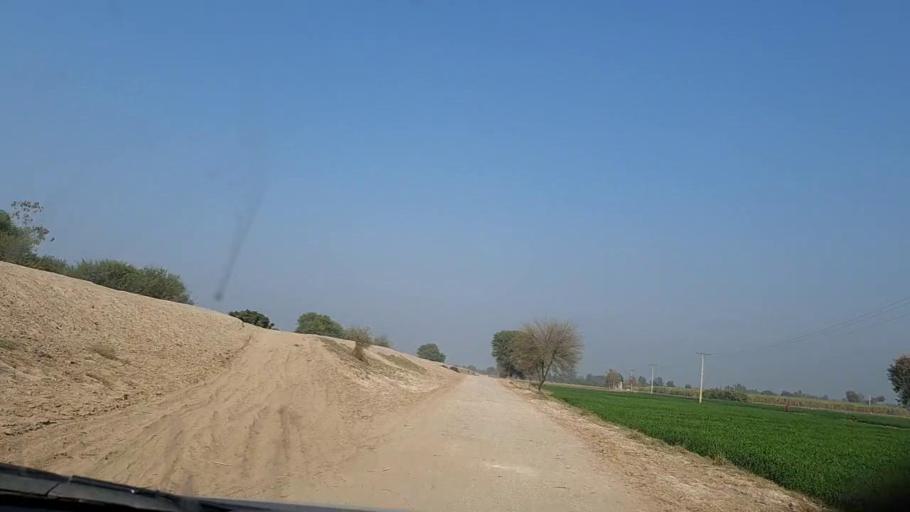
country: PK
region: Sindh
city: Moro
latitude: 26.8048
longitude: 67.9490
